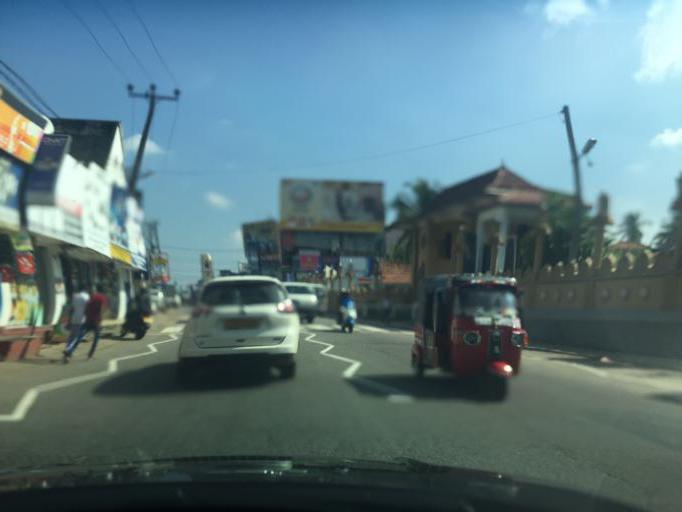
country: LK
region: Western
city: Maharagama
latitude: 6.8032
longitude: 79.9216
